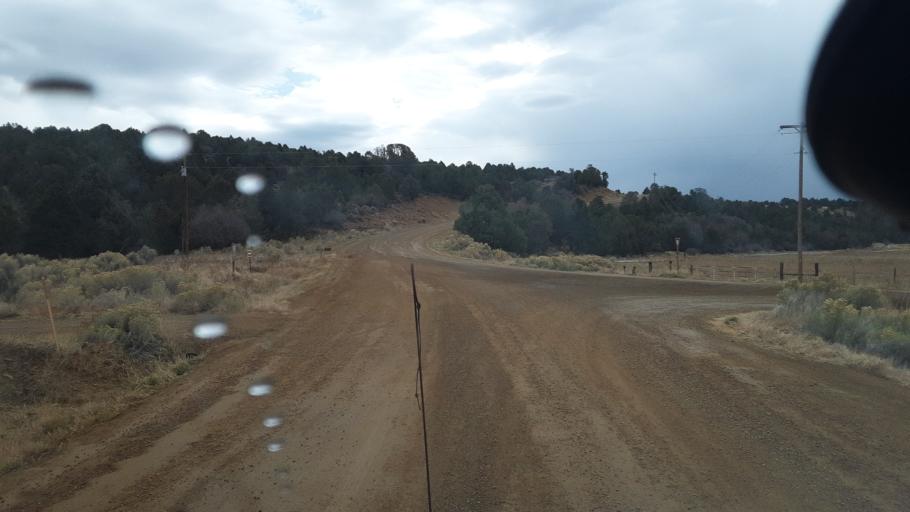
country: US
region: Colorado
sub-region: Montezuma County
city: Mancos
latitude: 37.2016
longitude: -108.1384
